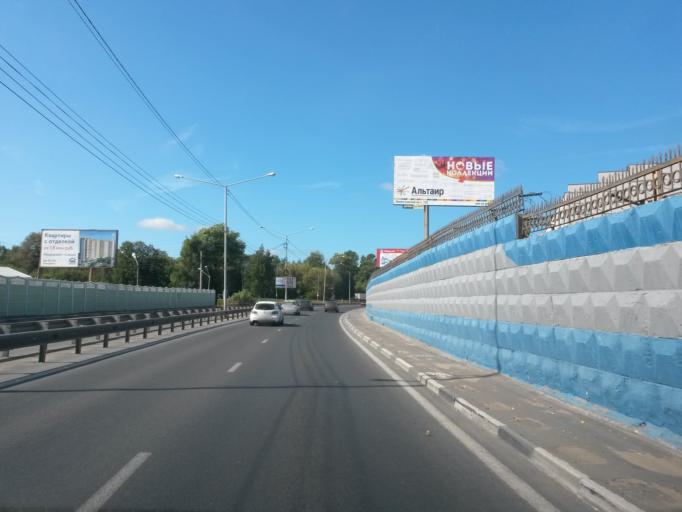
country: RU
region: Jaroslavl
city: Yaroslavl
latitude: 57.5976
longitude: 39.8884
